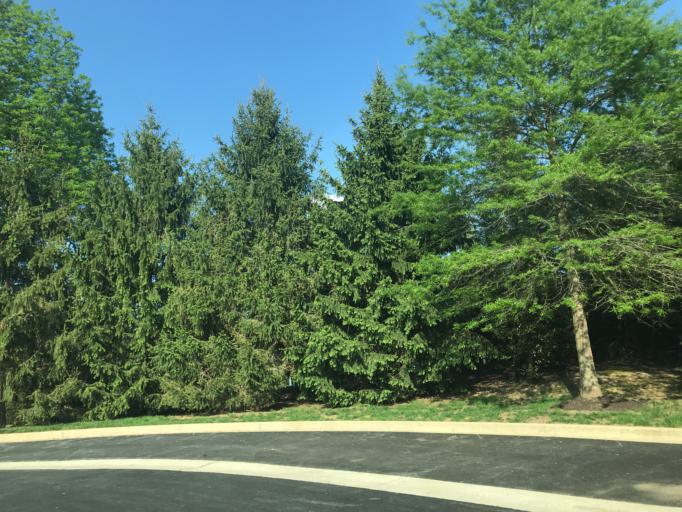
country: US
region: Maryland
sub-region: Baltimore County
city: Towson
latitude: 39.3842
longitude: -76.6213
